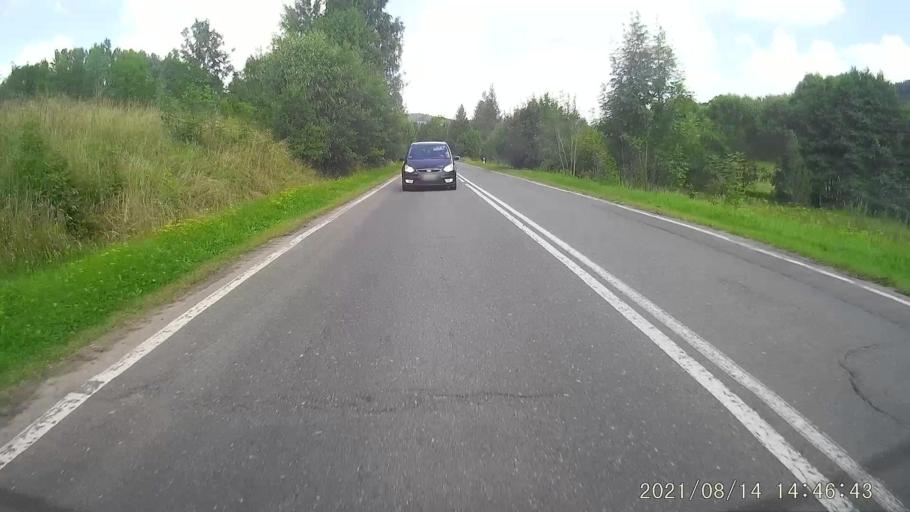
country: PL
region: Lower Silesian Voivodeship
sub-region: Powiat klodzki
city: Ludwikowice Klodzkie
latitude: 50.6304
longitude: 16.4165
